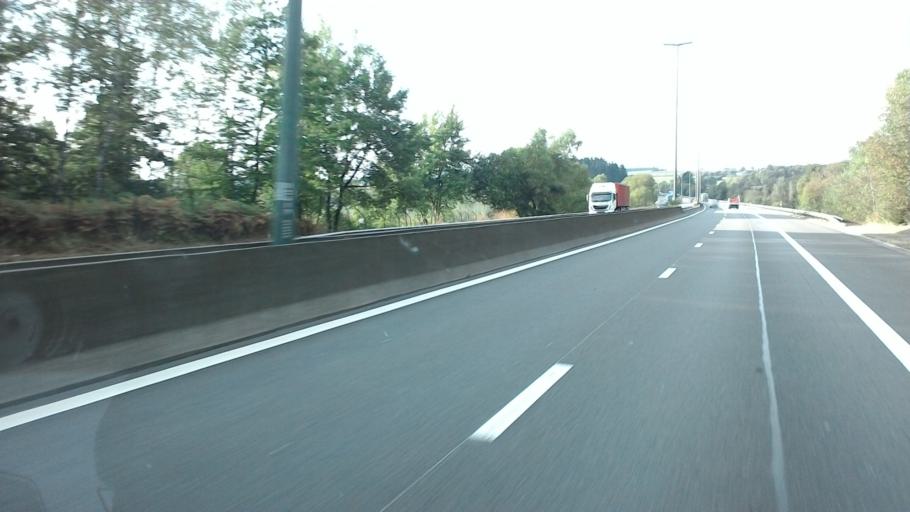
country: BE
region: Wallonia
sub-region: Province du Luxembourg
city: Leglise
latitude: 49.7645
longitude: 5.5591
